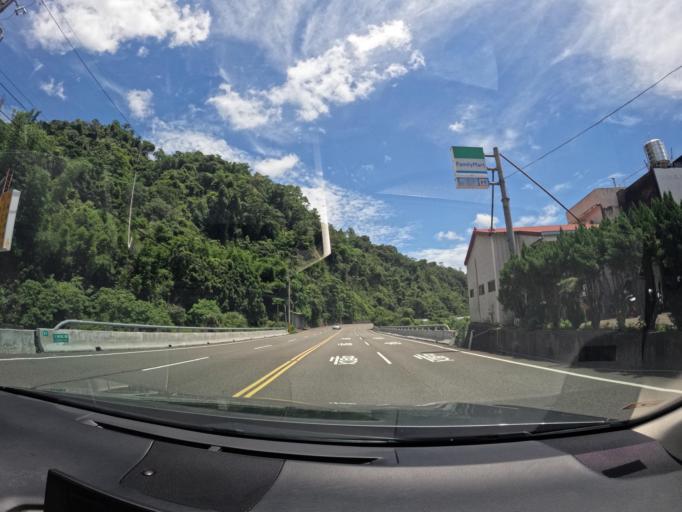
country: TW
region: Taiwan
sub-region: Miaoli
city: Miaoli
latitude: 24.5373
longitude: 120.9181
